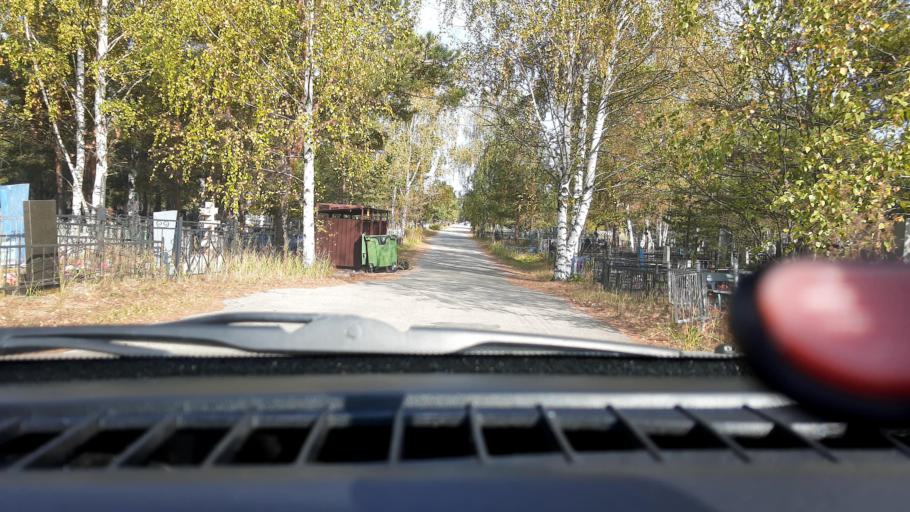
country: RU
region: Nizjnij Novgorod
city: Gorbatovka
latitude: 56.3586
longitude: 43.7669
